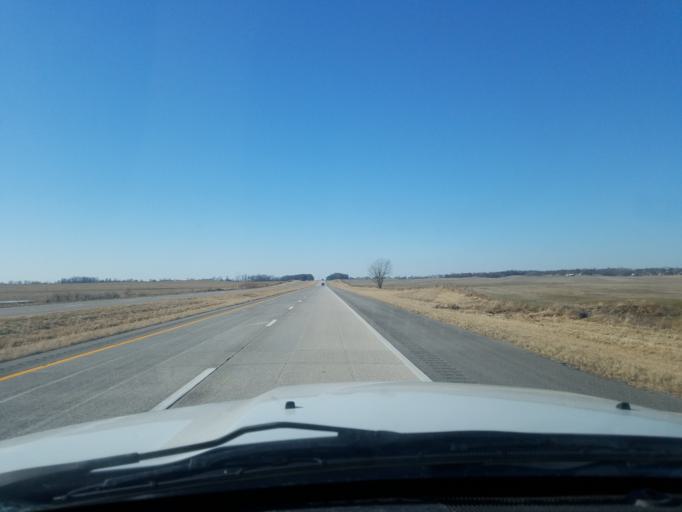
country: US
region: Kentucky
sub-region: Henderson County
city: Henderson
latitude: 37.8009
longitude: -87.5161
